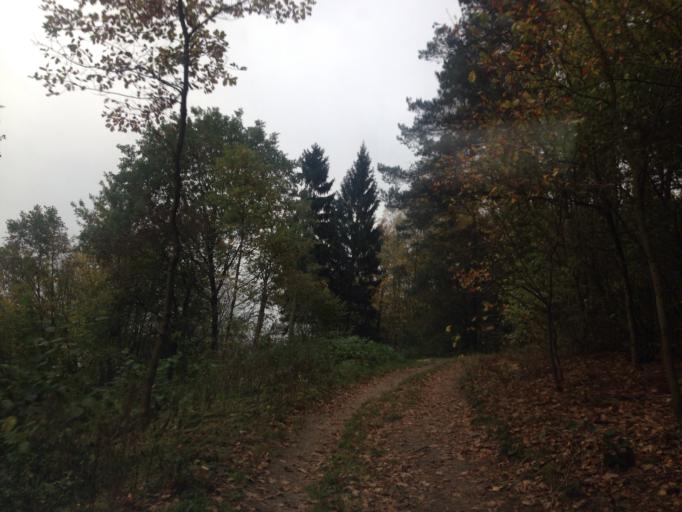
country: PL
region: Kujawsko-Pomorskie
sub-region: Powiat brodnicki
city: Bobrowo
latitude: 53.3192
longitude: 19.2414
